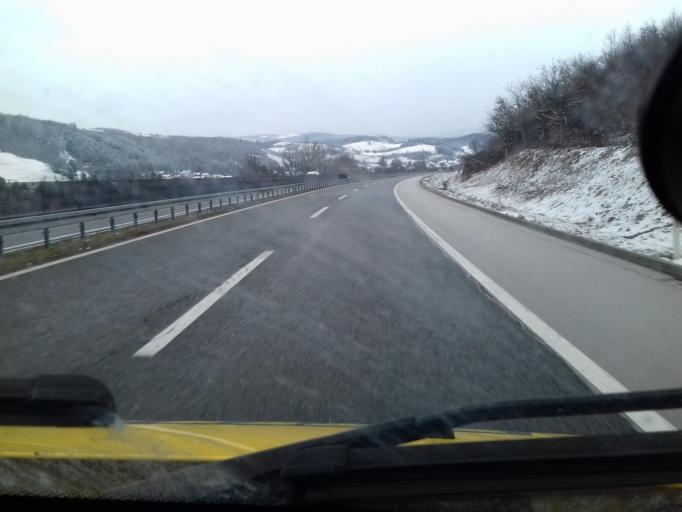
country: BA
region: Federation of Bosnia and Herzegovina
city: Visoko
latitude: 43.9930
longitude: 18.2134
